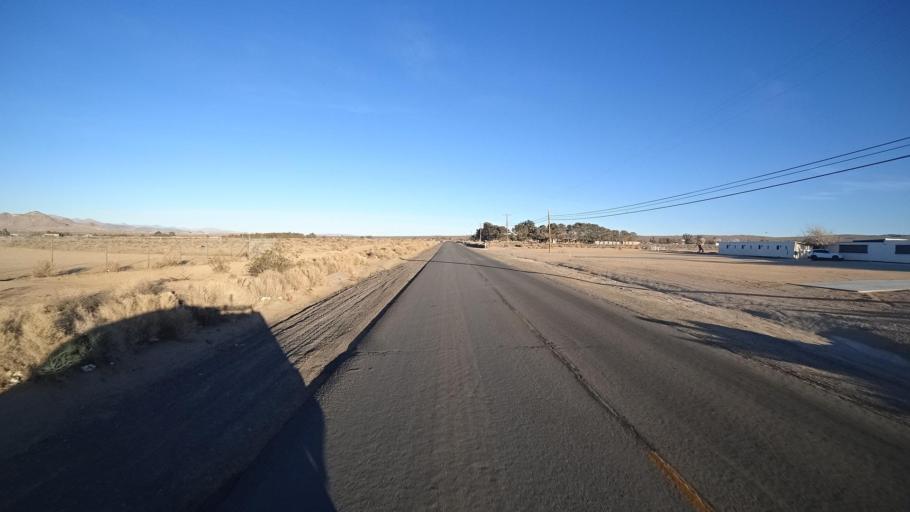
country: US
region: California
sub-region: Kern County
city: Ridgecrest
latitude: 35.6081
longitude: -117.6457
